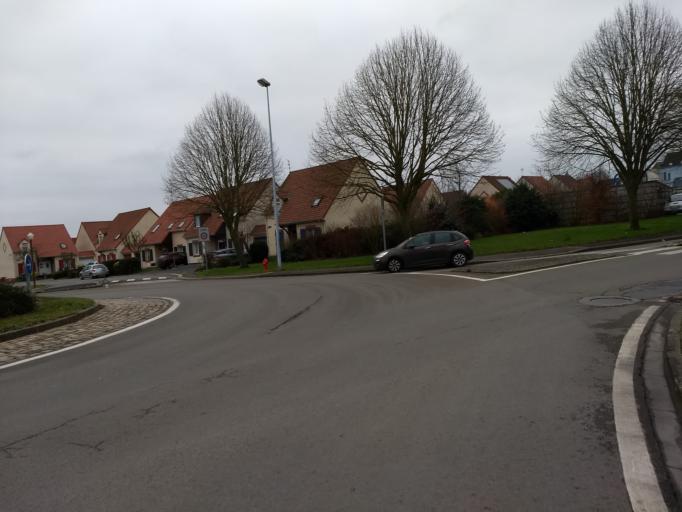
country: FR
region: Nord-Pas-de-Calais
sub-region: Departement du Pas-de-Calais
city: Saint-Laurent-Blangy
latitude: 50.2861
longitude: 2.7963
